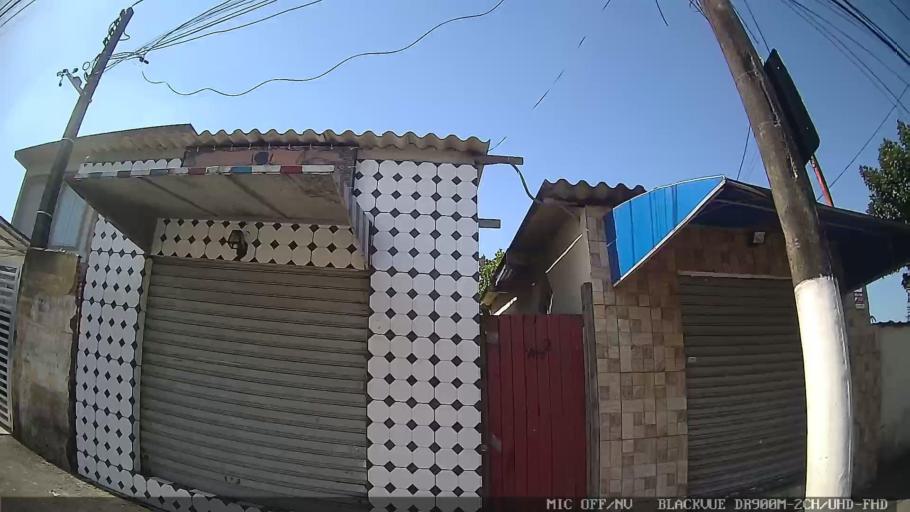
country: BR
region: Sao Paulo
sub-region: Santos
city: Santos
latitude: -23.9413
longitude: -46.2995
